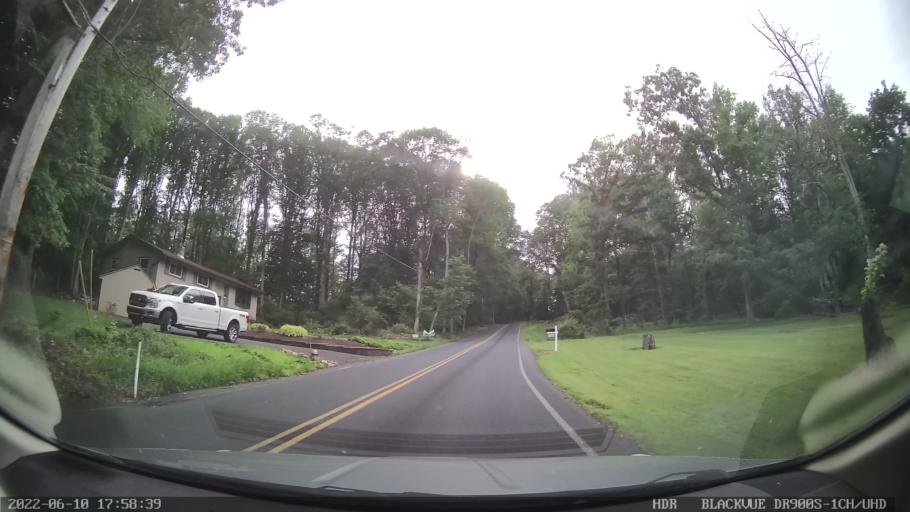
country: US
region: Pennsylvania
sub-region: Berks County
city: Pennside
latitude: 40.3395
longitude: -75.8891
